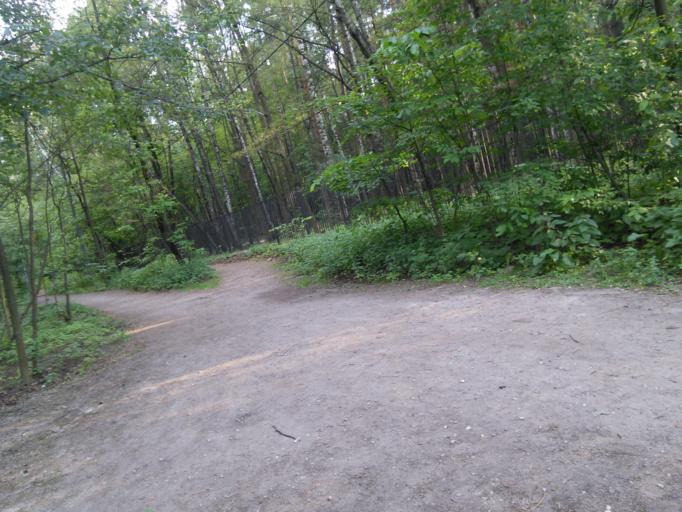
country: RU
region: Moscow
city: Sokol'niki
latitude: 55.8072
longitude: 37.6751
